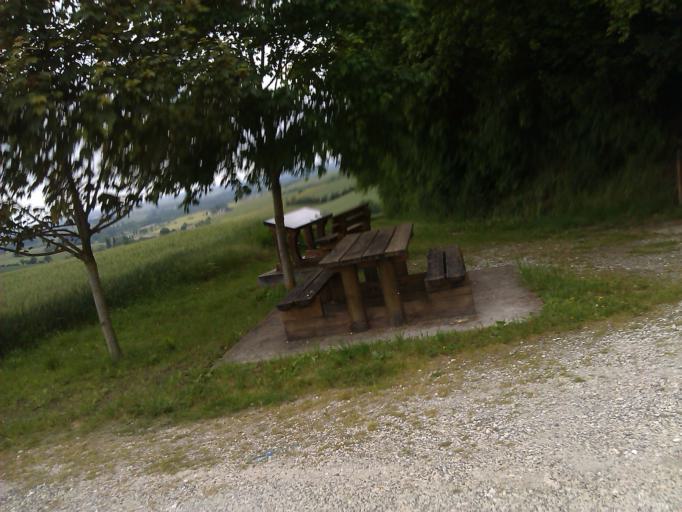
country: FR
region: Poitou-Charentes
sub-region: Departement de la Charente
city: Chateauneuf-sur-Charente
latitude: 45.5423
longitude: -0.0753
